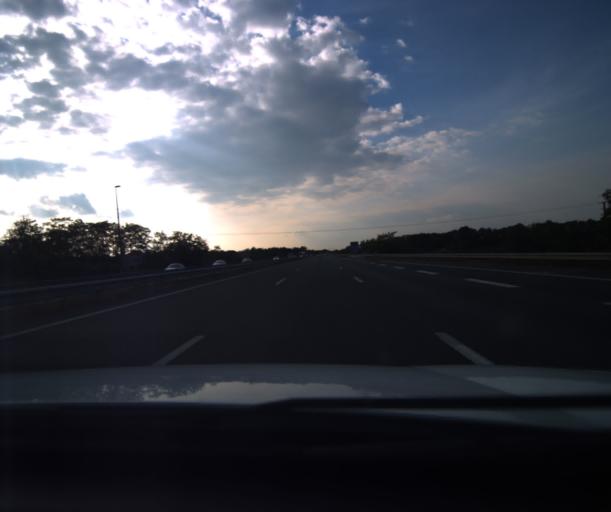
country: FR
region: Midi-Pyrenees
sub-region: Departement de la Haute-Garonne
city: Castelnau-d'Estretefonds
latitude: 43.8142
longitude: 1.3576
